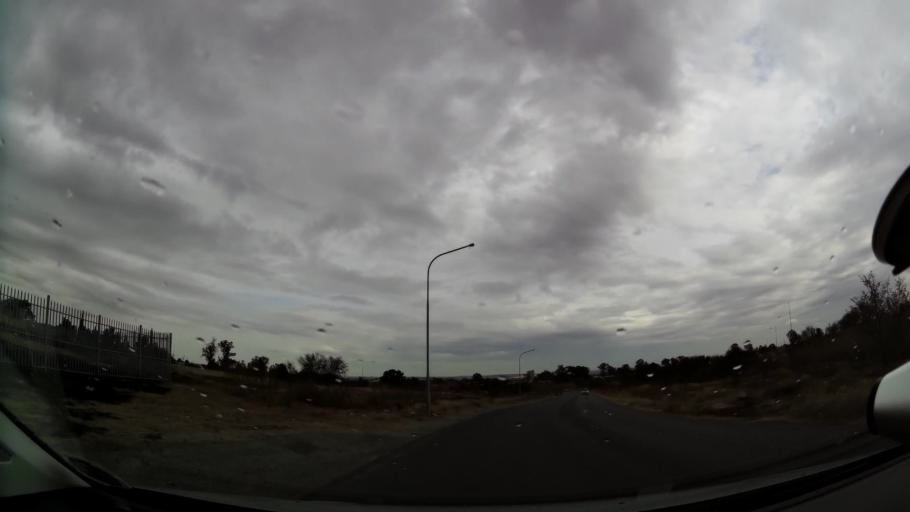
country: ZA
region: Orange Free State
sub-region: Fezile Dabi District Municipality
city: Kroonstad
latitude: -27.6486
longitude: 27.2286
